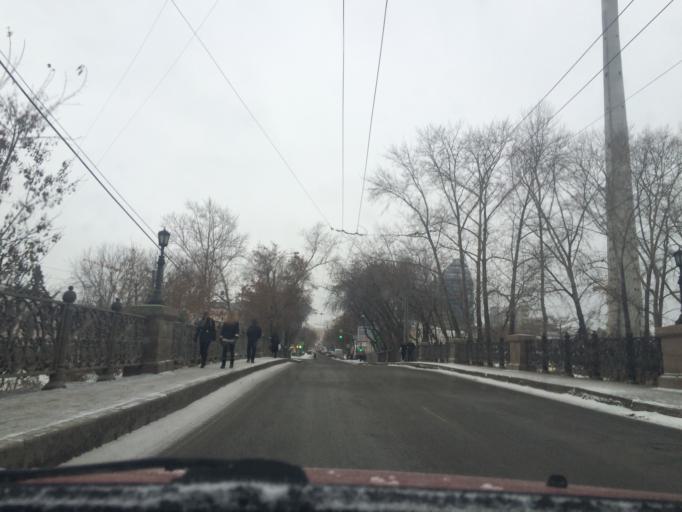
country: RU
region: Sverdlovsk
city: Yekaterinburg
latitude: 56.8236
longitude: 60.6140
